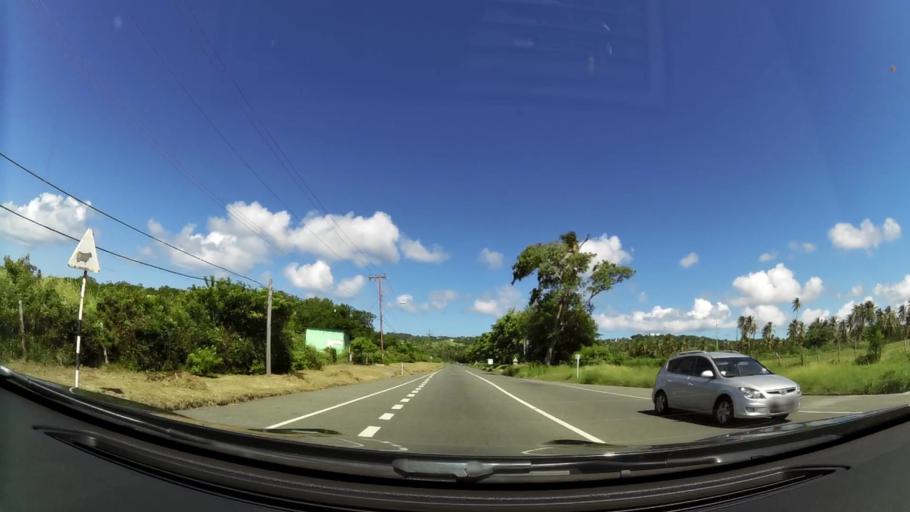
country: TT
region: Tobago
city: Scarborough
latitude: 11.1644
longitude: -60.7715
